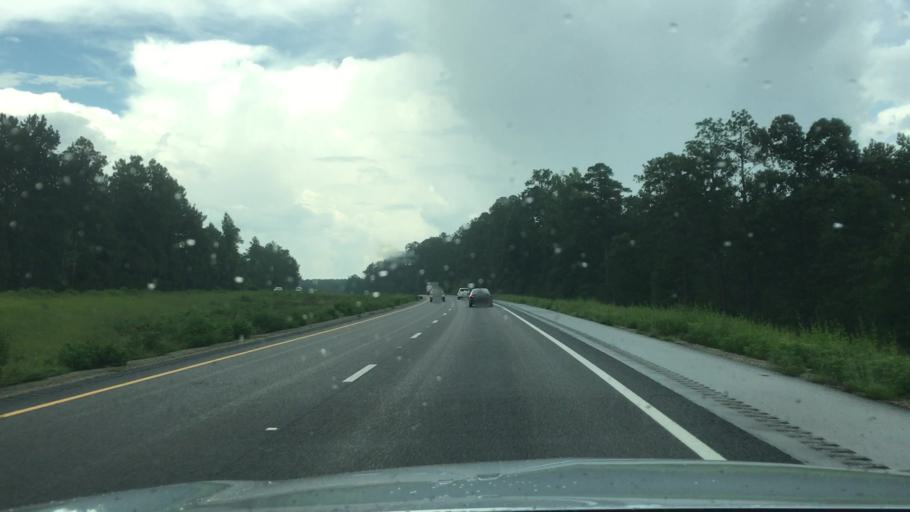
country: US
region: Mississippi
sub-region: Forrest County
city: Hattiesburg
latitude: 31.2271
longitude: -89.3233
